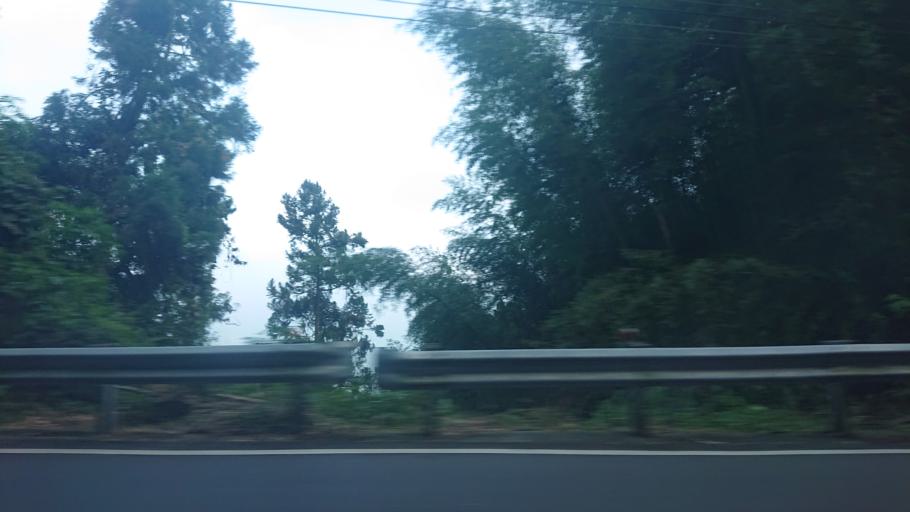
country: TW
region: Taiwan
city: Lugu
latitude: 23.4854
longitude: 120.7456
